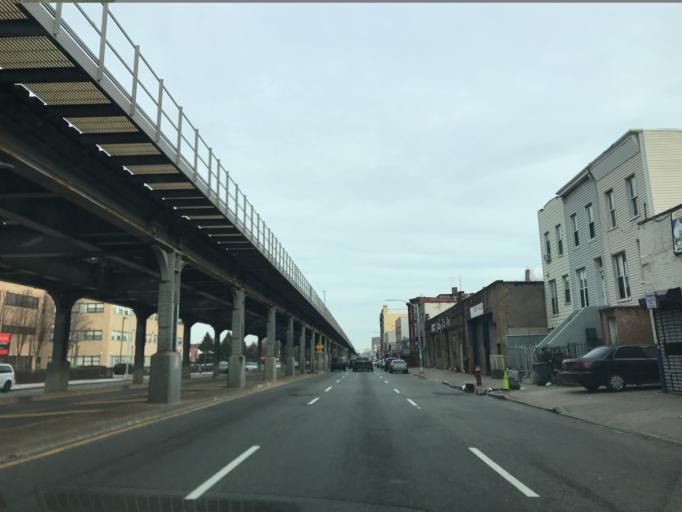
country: US
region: New York
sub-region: Kings County
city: Brooklyn
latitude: 40.6778
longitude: -73.9384
